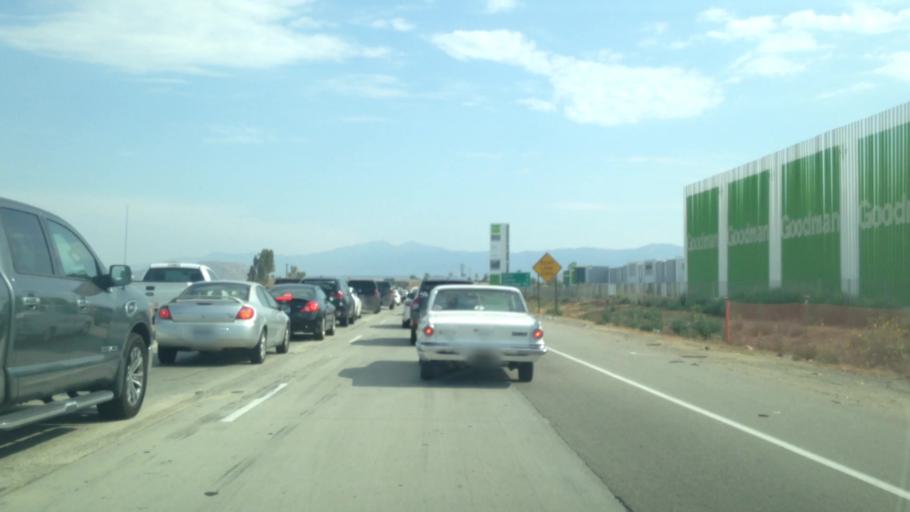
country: US
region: California
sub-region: Riverside County
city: Mira Loma
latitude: 33.9963
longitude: -117.5506
